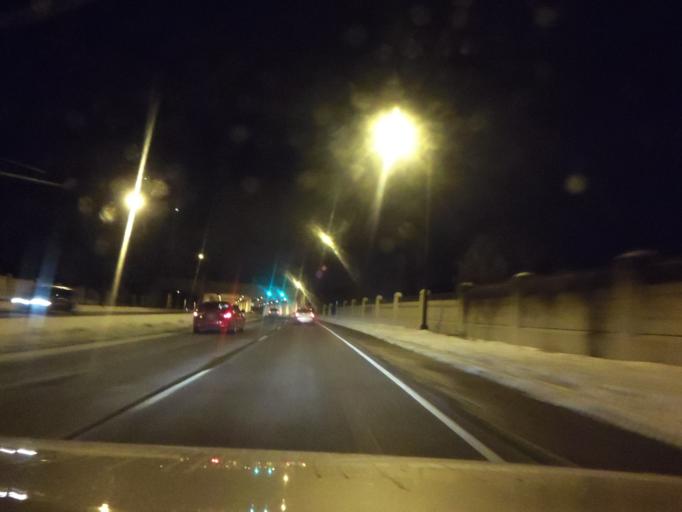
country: US
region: Minnesota
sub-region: Hennepin County
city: Richfield
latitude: 44.9145
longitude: -93.2121
